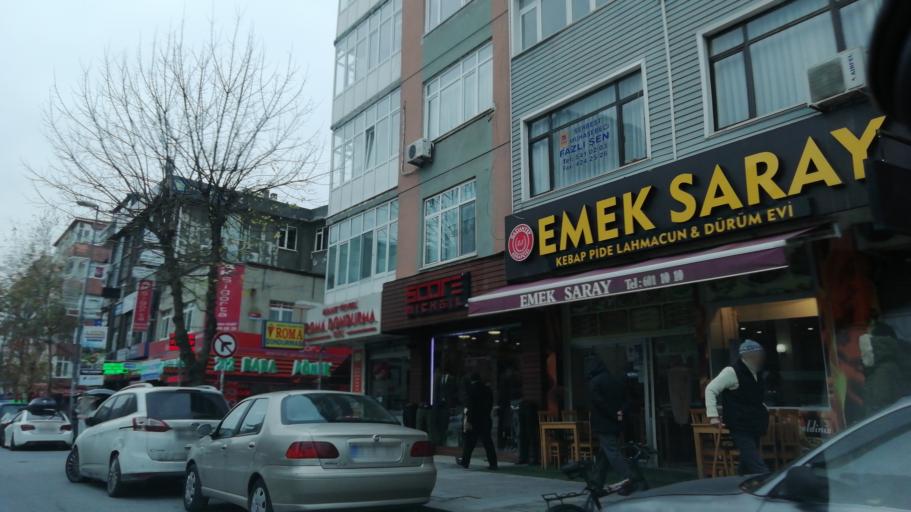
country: TR
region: Istanbul
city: Mahmutbey
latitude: 41.0019
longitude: 28.7976
